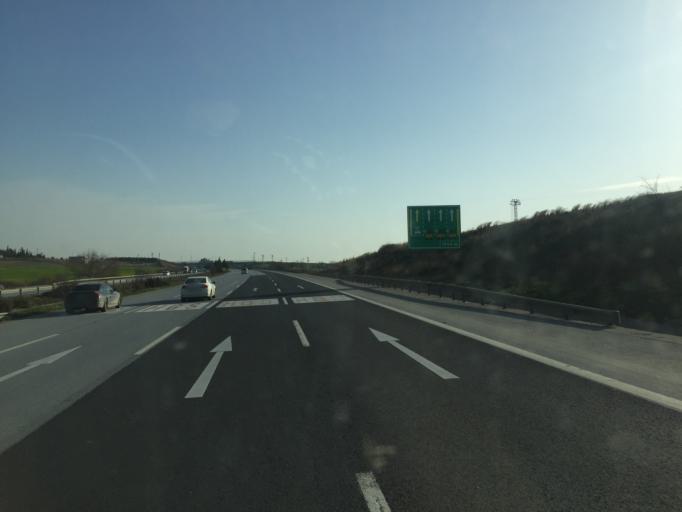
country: TR
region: Mersin
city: Yenice
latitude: 37.0236
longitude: 35.0983
